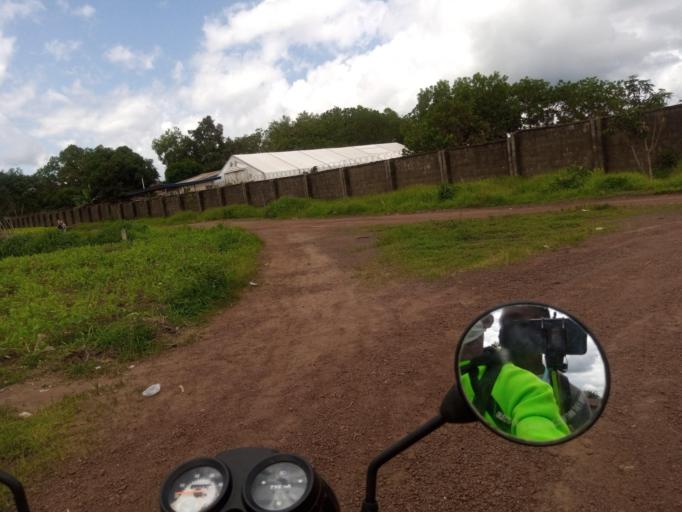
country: SL
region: Northern Province
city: Port Loko
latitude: 8.7750
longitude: -12.7725
